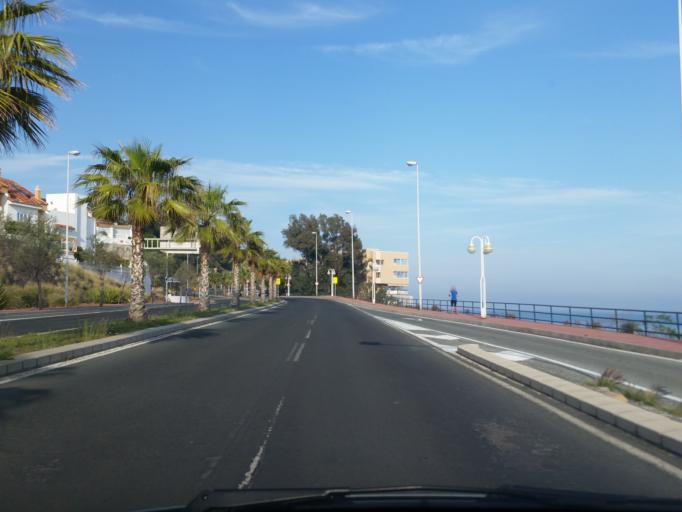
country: ES
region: Andalusia
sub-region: Provincia de Malaga
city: Benalmadena
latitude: 36.5763
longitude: -4.5763
